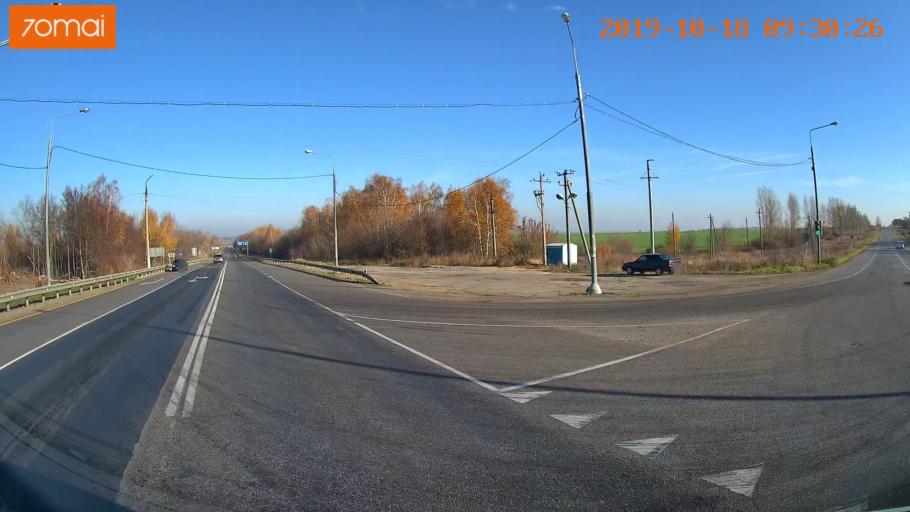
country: RU
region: Tula
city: Yefremov
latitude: 53.1392
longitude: 38.1596
